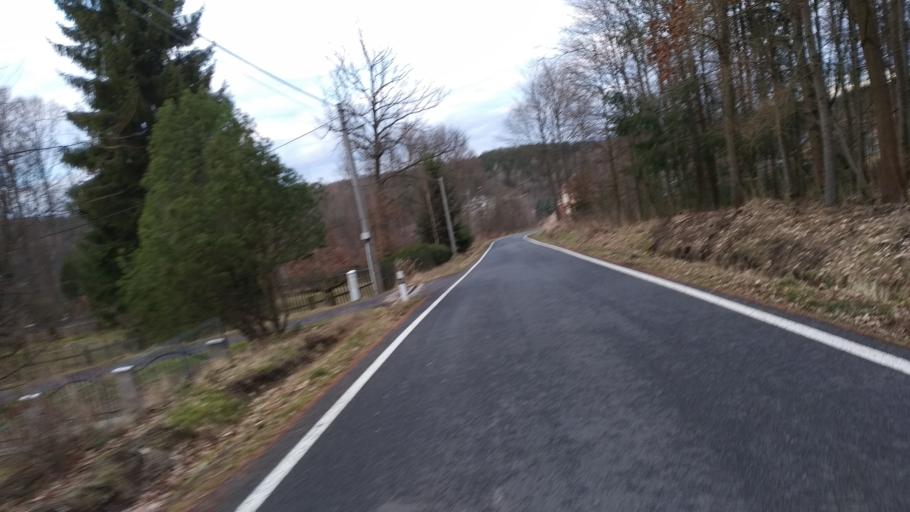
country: CZ
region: Karlovarsky
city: Kynsperk nad Ohri
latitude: 50.1266
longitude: 12.5503
